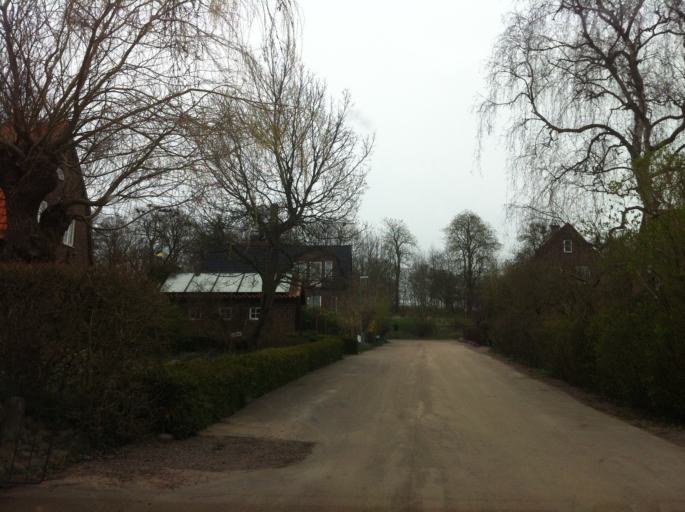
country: SE
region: Skane
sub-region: Svalovs Kommun
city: Kagerod
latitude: 55.9699
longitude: 13.0850
